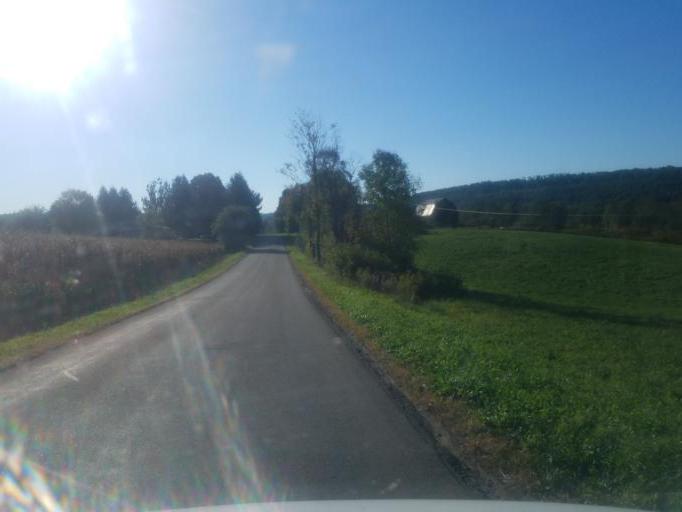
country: US
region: New York
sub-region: Allegany County
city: Cuba
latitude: 42.2544
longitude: -78.2469
